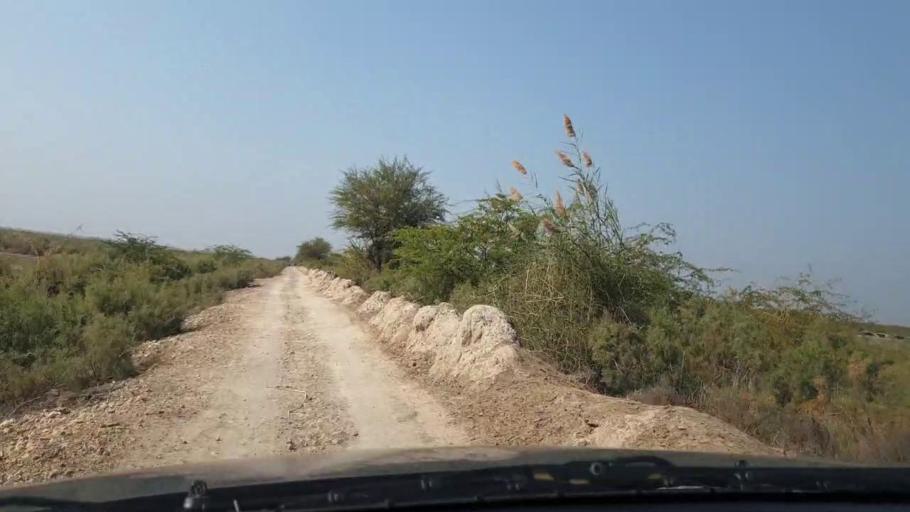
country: PK
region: Sindh
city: Jhol
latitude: 25.8873
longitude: 68.9826
